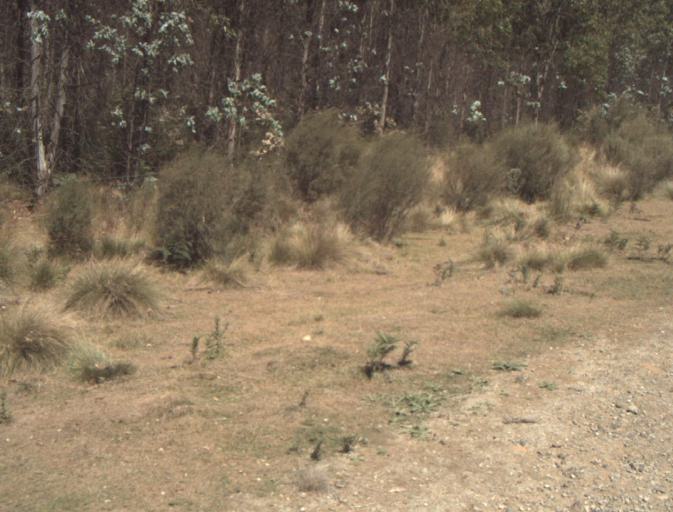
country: AU
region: Tasmania
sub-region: Dorset
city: Scottsdale
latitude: -41.3046
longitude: 147.4675
